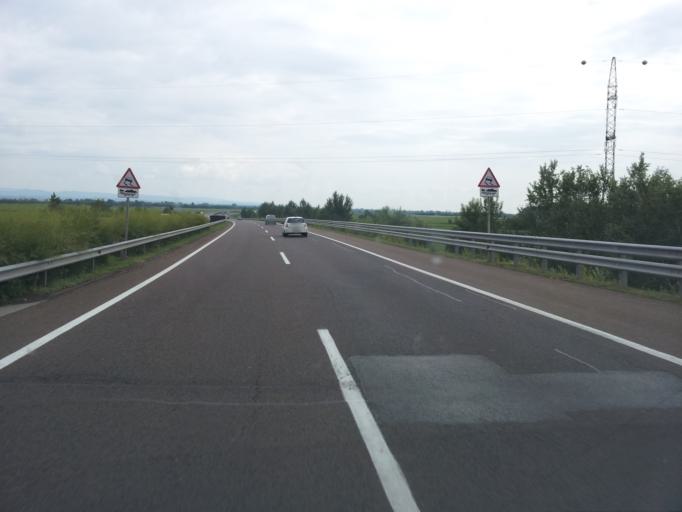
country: HU
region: Heves
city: Fuzesabony
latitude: 47.7418
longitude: 20.4436
